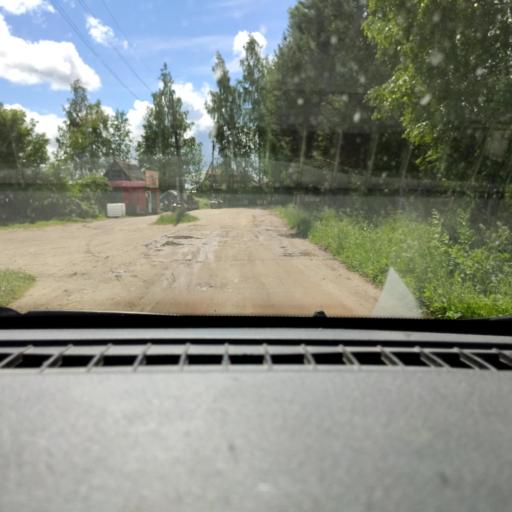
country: RU
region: Perm
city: Overyata
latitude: 58.1408
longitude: 55.8224
